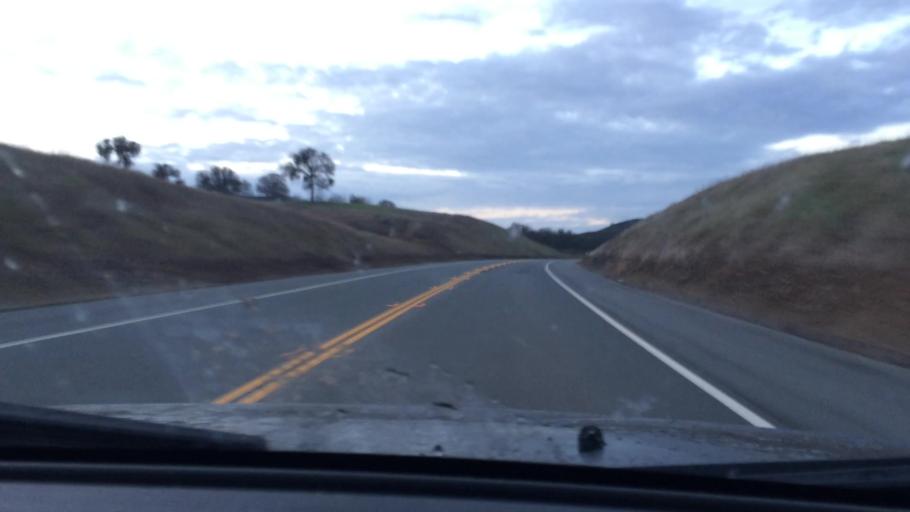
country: US
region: California
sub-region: Amador County
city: Plymouth
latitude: 38.4238
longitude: -120.8765
